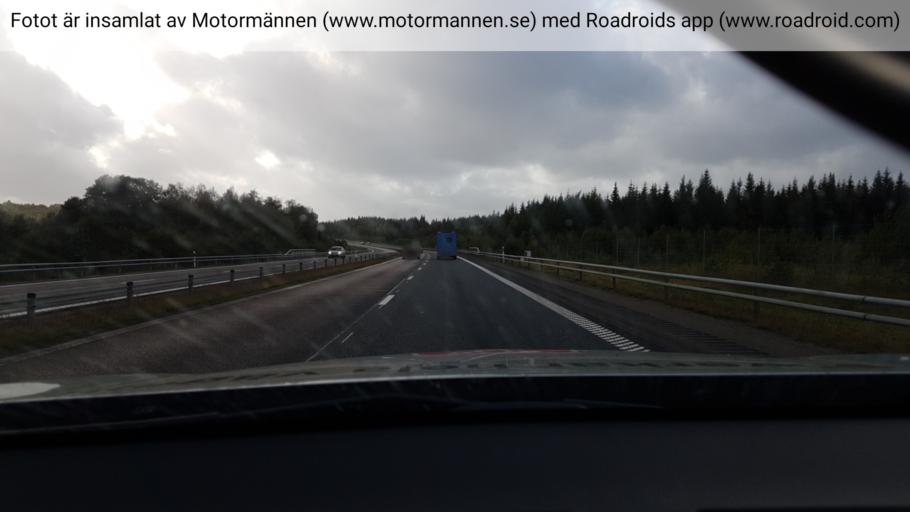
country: SE
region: Vaestra Goetaland
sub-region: Boras Kommun
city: Dalsjofors
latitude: 57.8088
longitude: 13.2004
